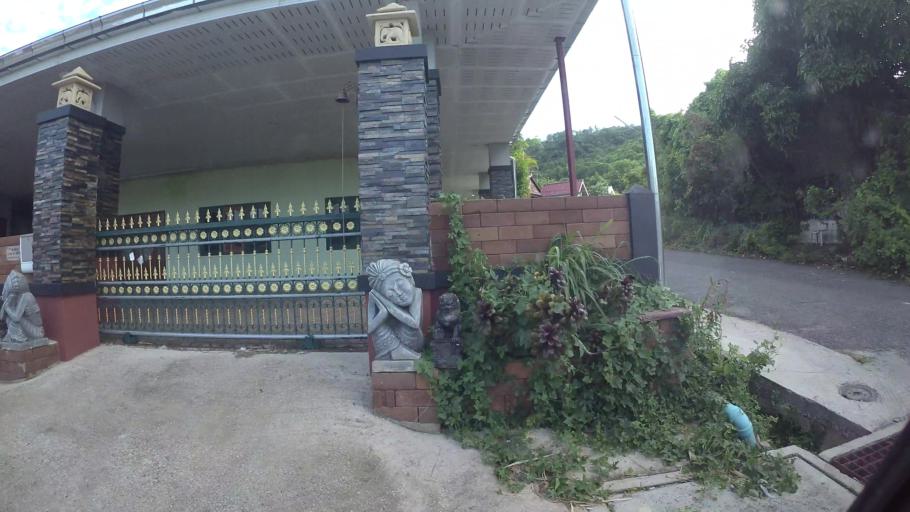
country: TH
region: Chon Buri
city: Sattahip
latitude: 12.6918
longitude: 100.9249
